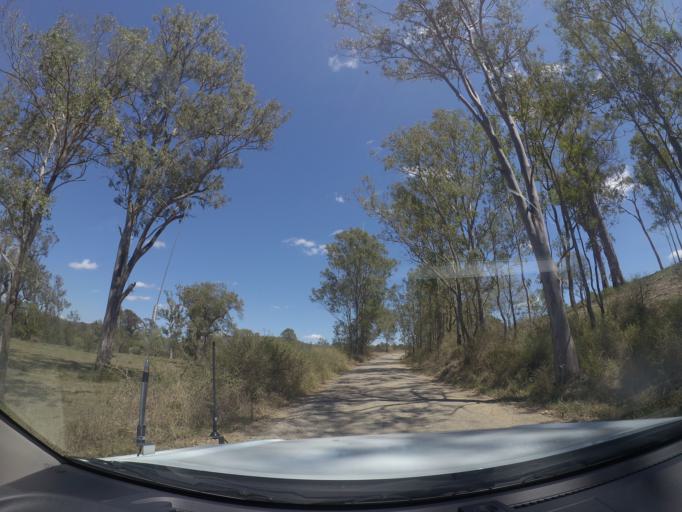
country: AU
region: Queensland
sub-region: Logan
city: Cedar Vale
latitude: -27.8478
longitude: 152.8841
